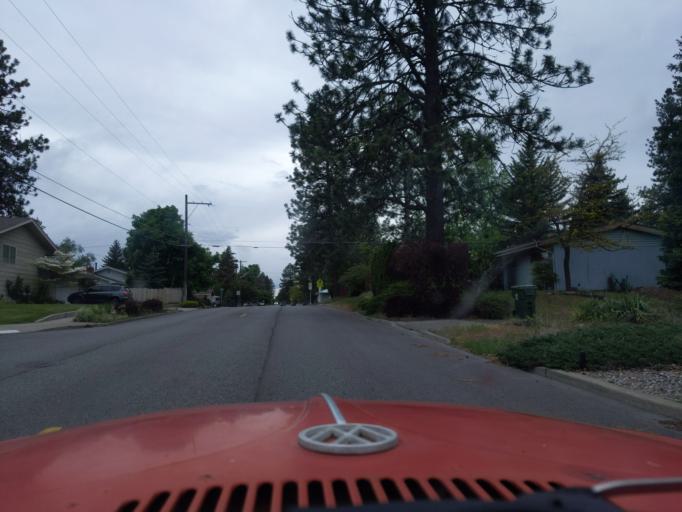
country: US
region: Washington
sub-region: Spokane County
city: Spokane
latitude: 47.6173
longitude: -117.3765
